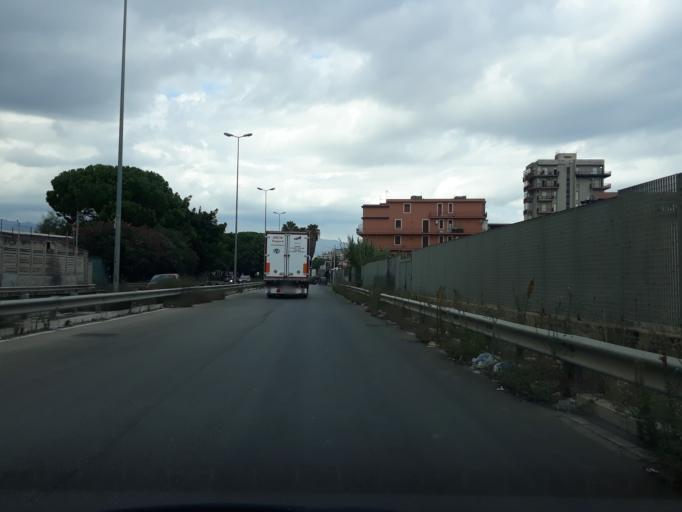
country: IT
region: Sicily
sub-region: Palermo
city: Ciaculli
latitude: 38.0934
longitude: 13.4048
